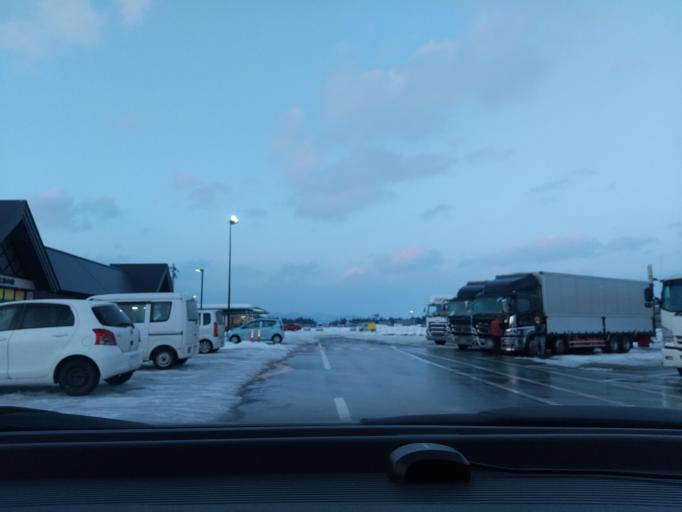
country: JP
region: Iwate
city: Hanamaki
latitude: 39.3660
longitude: 141.0562
